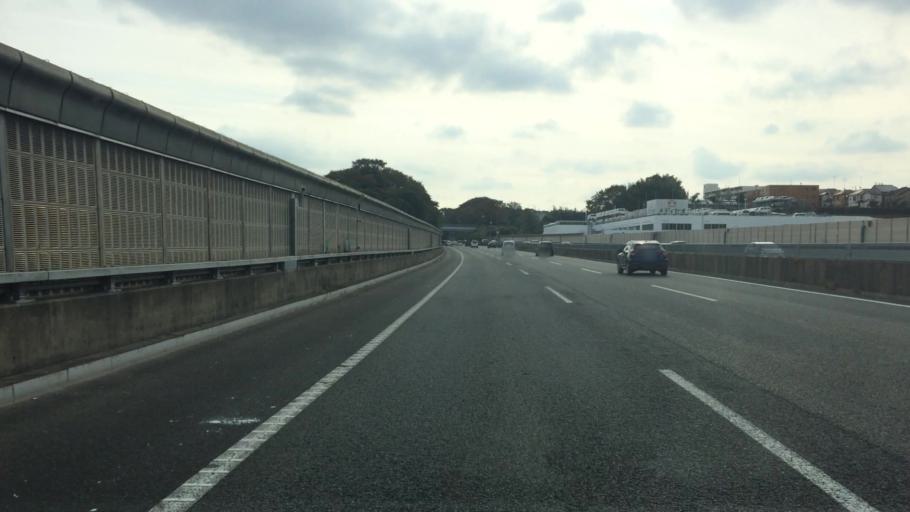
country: JP
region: Tokyo
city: Chofugaoka
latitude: 35.5851
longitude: 139.6201
